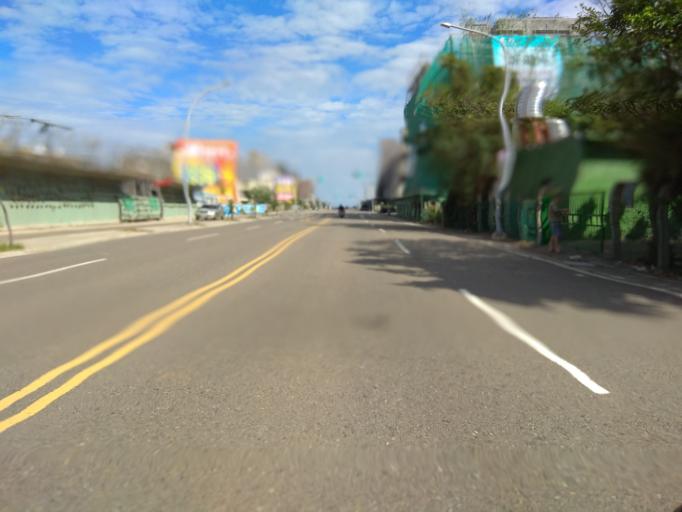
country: TW
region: Taiwan
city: Taoyuan City
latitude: 25.0465
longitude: 121.1369
